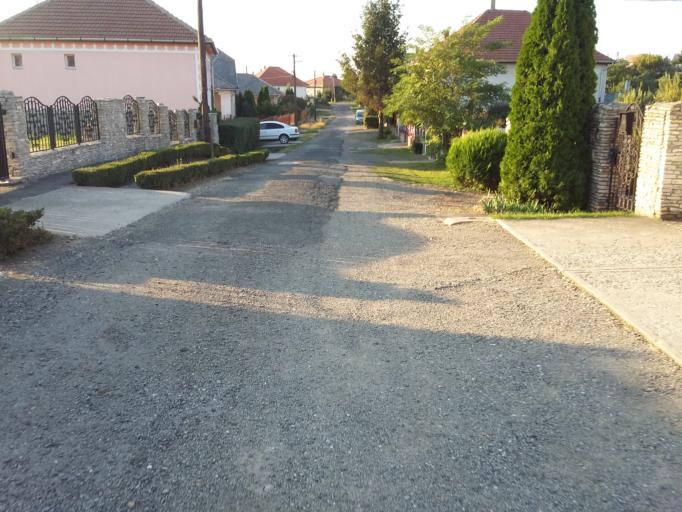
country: HU
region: Borsod-Abauj-Zemplen
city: Bekecs
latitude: 48.1608
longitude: 21.1790
